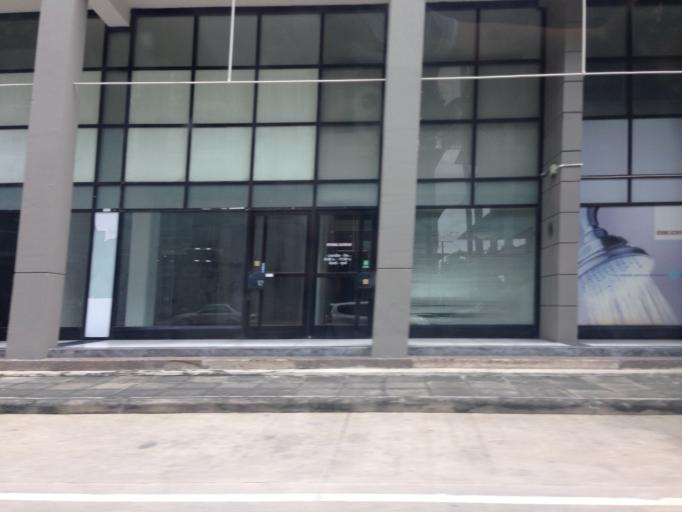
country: TH
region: Nonthaburi
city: Pak Kret
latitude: 13.9236
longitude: 100.5365
